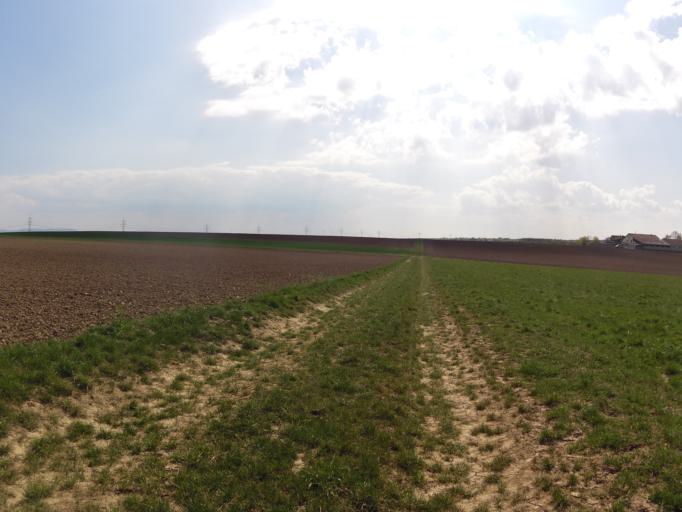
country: DE
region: Bavaria
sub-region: Regierungsbezirk Unterfranken
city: Oberpleichfeld
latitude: 49.8471
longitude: 10.0761
